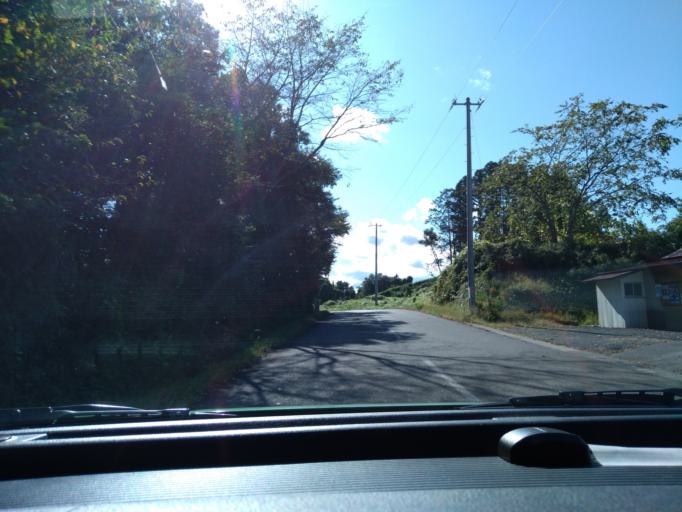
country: JP
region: Iwate
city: Ichinoseki
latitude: 38.7836
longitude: 141.2069
